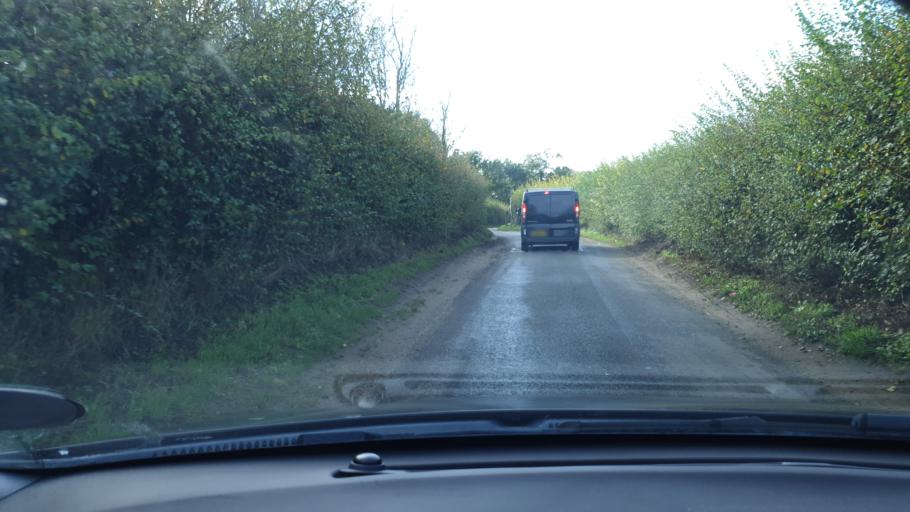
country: GB
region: England
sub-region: Essex
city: Alresford
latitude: 51.8596
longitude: 1.0232
